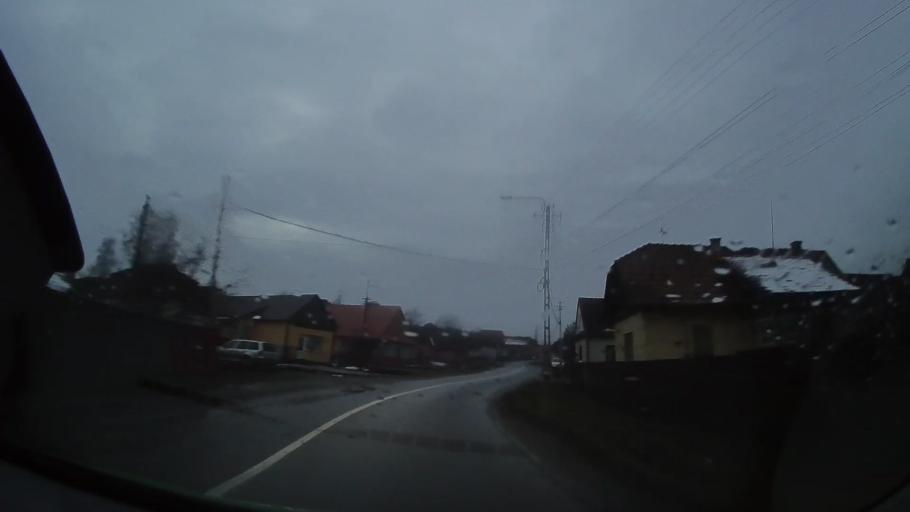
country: RO
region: Harghita
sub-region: Comuna Remetea
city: Remetea
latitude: 46.7927
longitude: 25.4494
